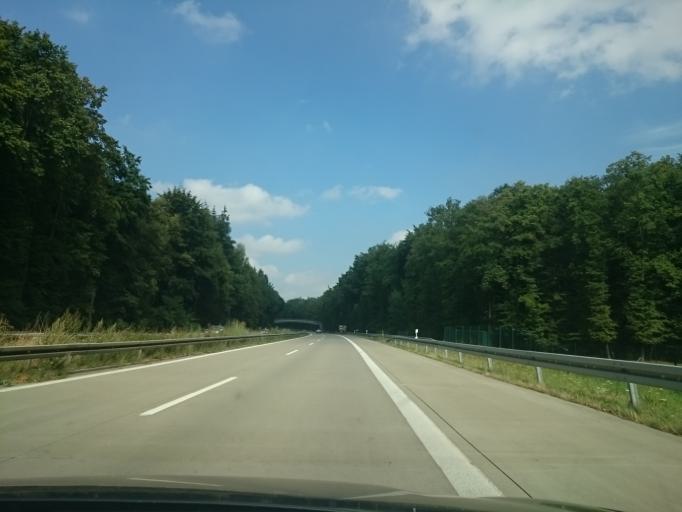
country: DE
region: Brandenburg
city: Gramzow
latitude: 53.1421
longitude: 13.8944
